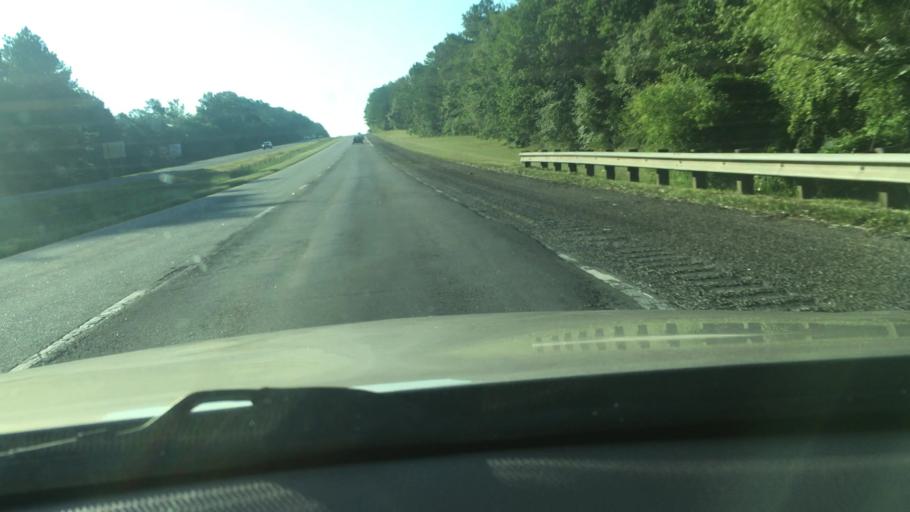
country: US
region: South Carolina
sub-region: Richland County
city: Lake Murray of Richland
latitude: 34.1577
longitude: -81.2682
